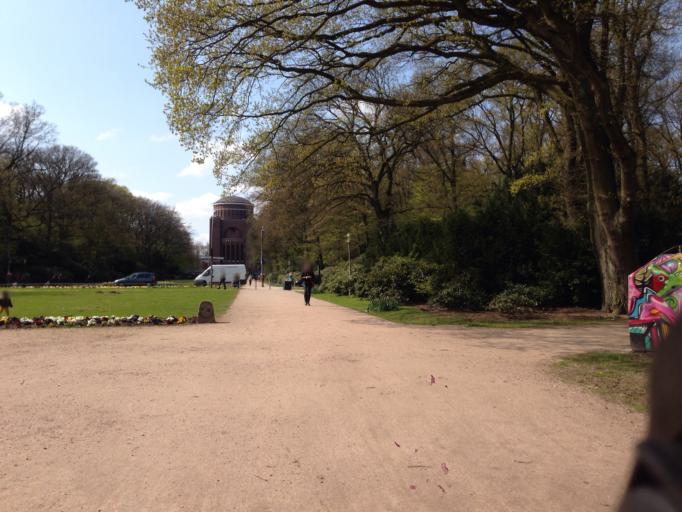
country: DE
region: Hamburg
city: Alsterdorf
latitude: 53.5960
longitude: 10.0149
